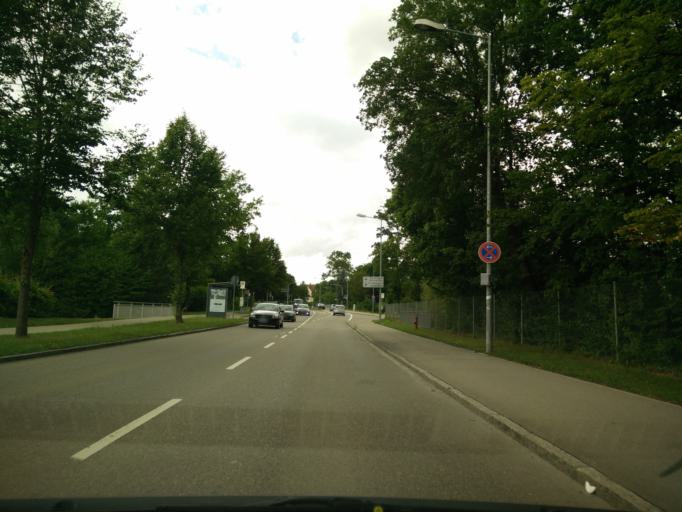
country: DE
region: Baden-Wuerttemberg
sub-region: Freiburg Region
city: Bad Durrheim
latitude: 48.0525
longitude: 8.5305
